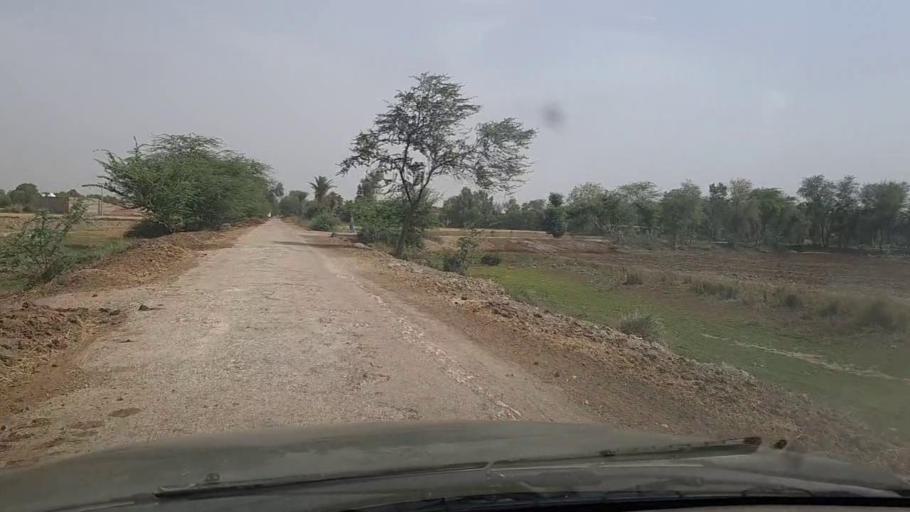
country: PK
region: Sindh
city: Lakhi
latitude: 27.8438
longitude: 68.7593
